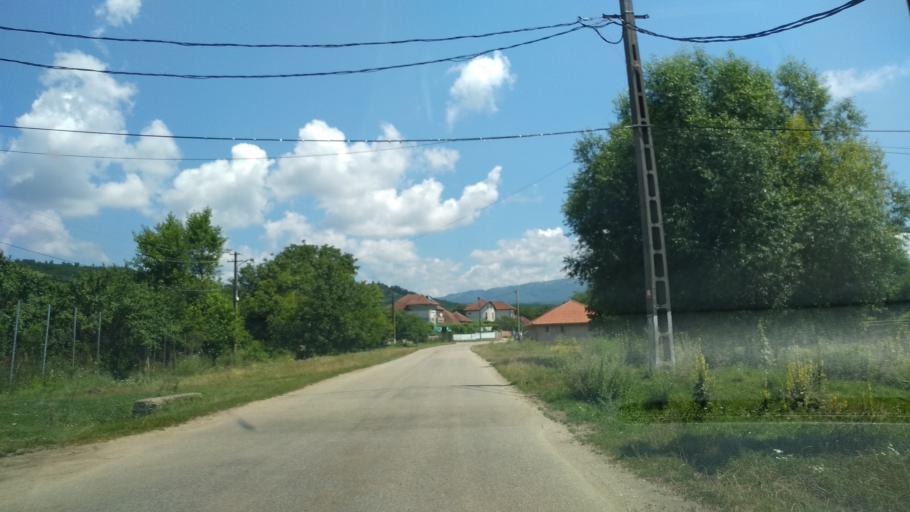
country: RO
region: Hunedoara
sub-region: Comuna Bosorod
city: Bosorod
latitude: 45.7057
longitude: 23.0627
